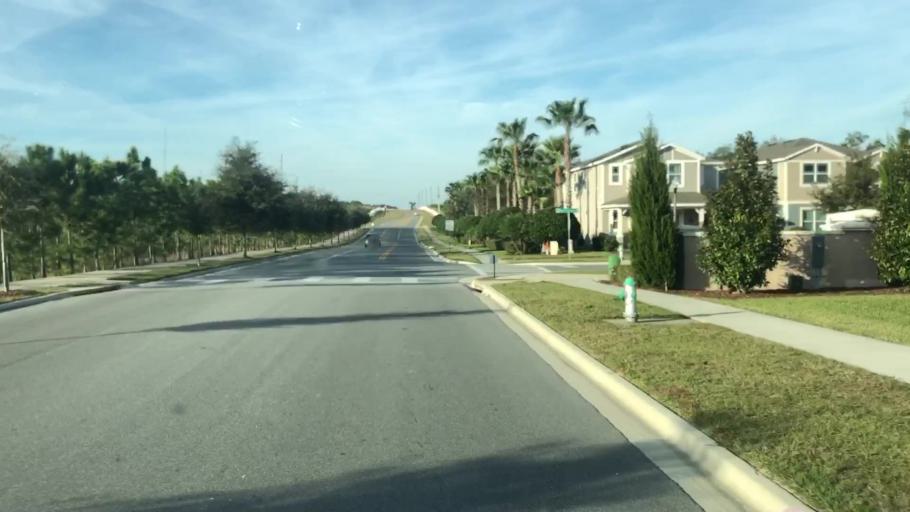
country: US
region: Florida
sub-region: Orange County
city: Lake Butler
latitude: 28.4396
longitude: -81.6237
